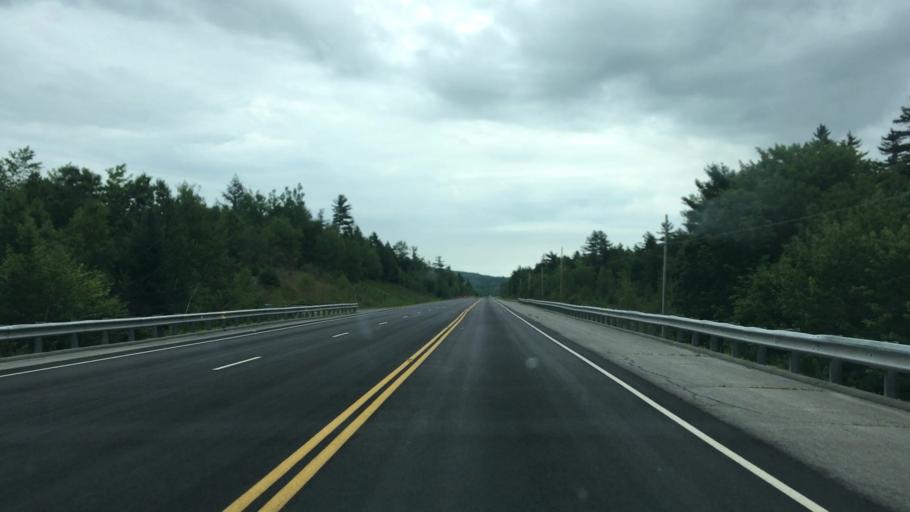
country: US
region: Maine
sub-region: Washington County
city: Cherryfield
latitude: 44.8752
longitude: -67.8957
